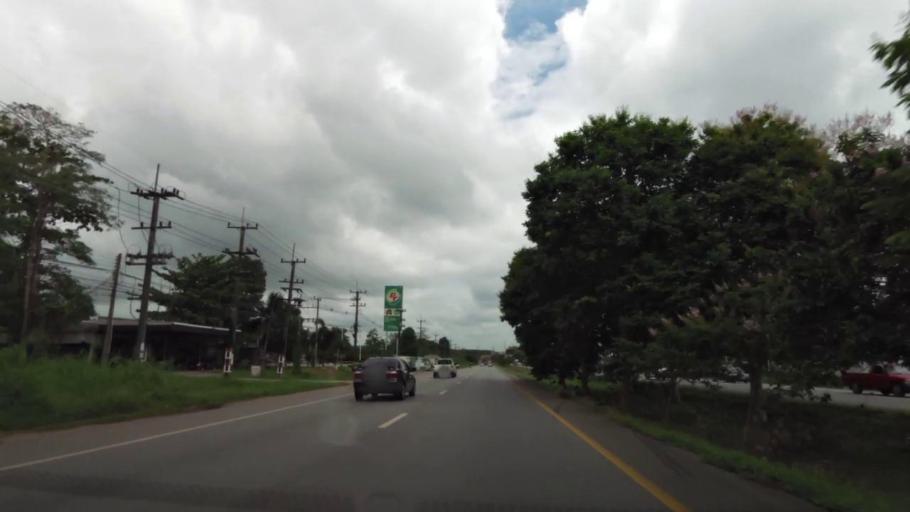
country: TH
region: Chanthaburi
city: Na Yai Am
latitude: 12.7719
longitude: 101.8425
